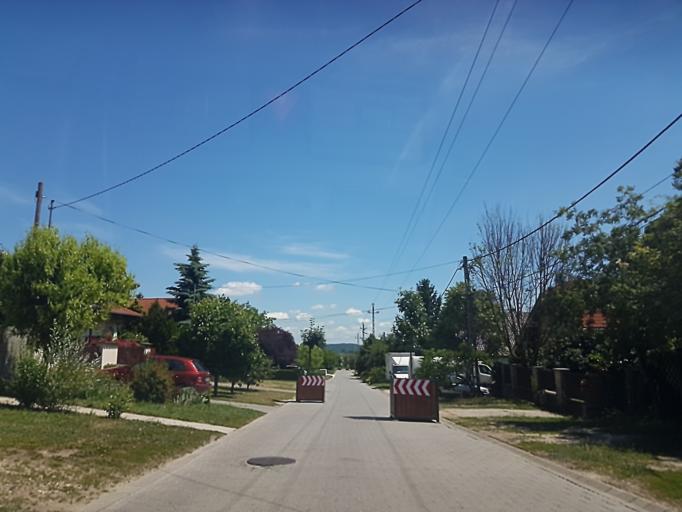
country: HU
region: Pest
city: Pilisvorosvar
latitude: 47.6099
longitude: 18.9069
